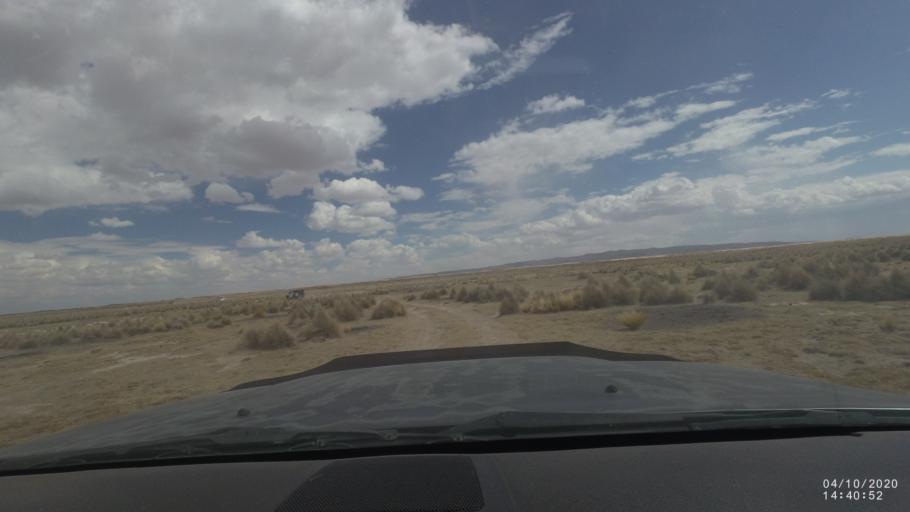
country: BO
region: Oruro
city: Poopo
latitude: -18.6807
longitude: -67.4913
